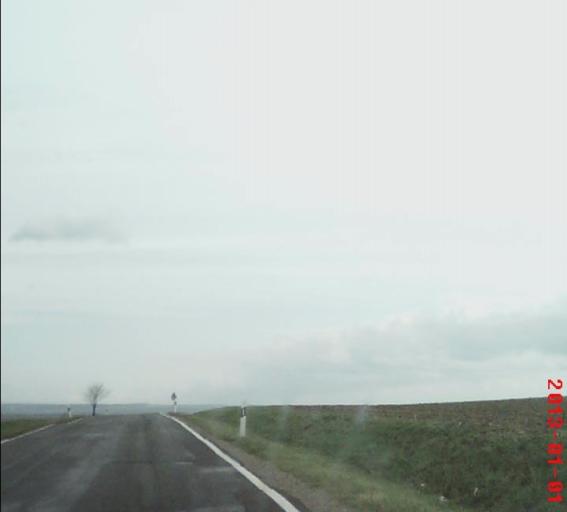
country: DE
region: Thuringia
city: Anrode
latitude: 51.2353
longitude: 10.3900
